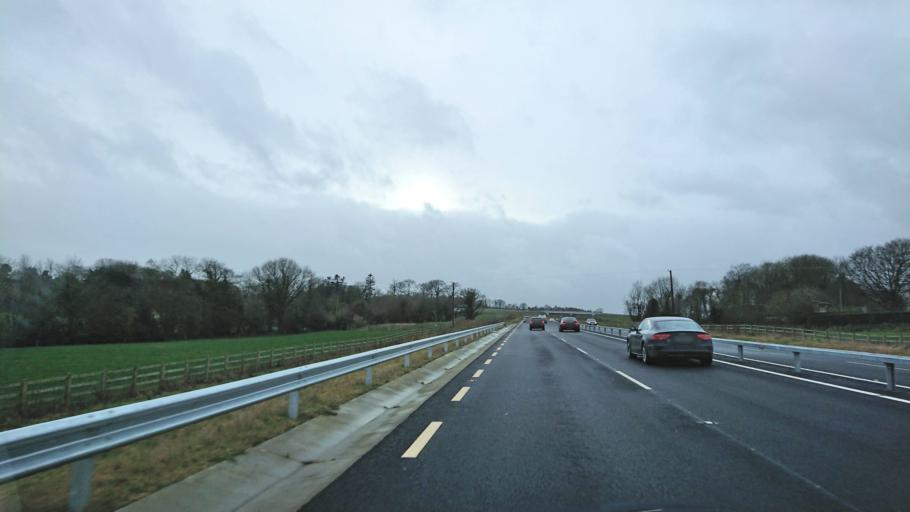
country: IE
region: Leinster
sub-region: Loch Garman
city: New Ross
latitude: 52.3769
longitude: -6.9148
